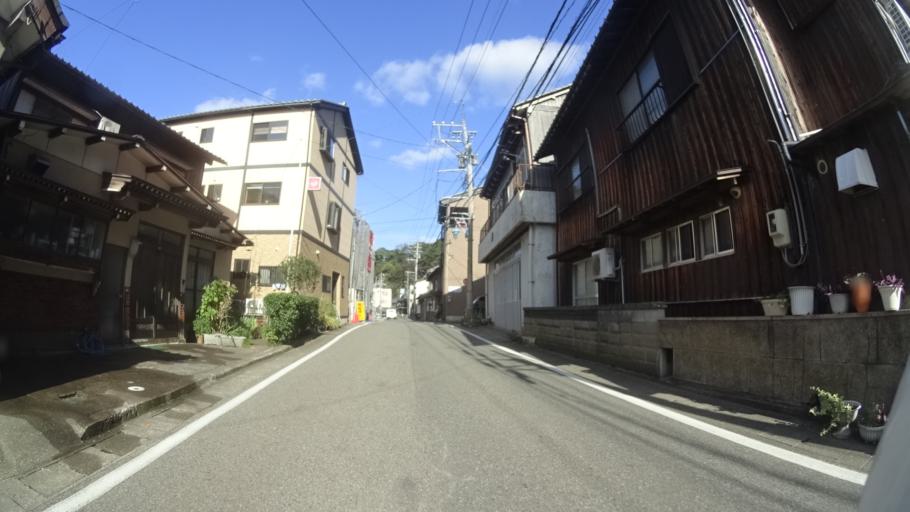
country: JP
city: Asahi
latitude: 35.9377
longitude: 135.9957
